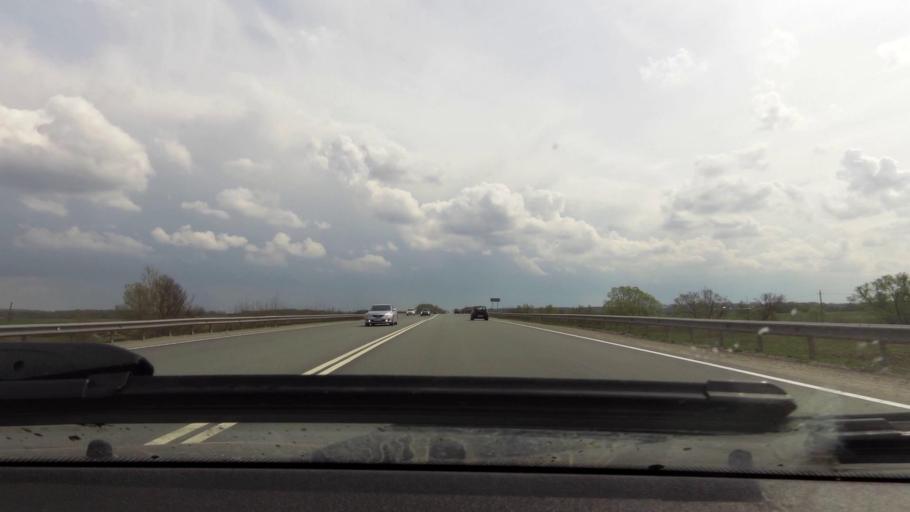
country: RU
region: Rjazan
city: Bagramovo
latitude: 54.7446
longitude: 39.4370
